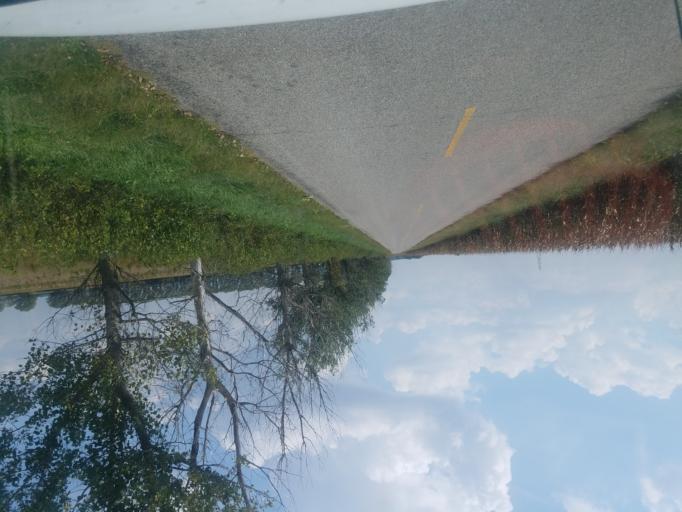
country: US
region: Ohio
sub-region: Hardin County
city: Ada
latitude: 40.6392
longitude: -83.7900
